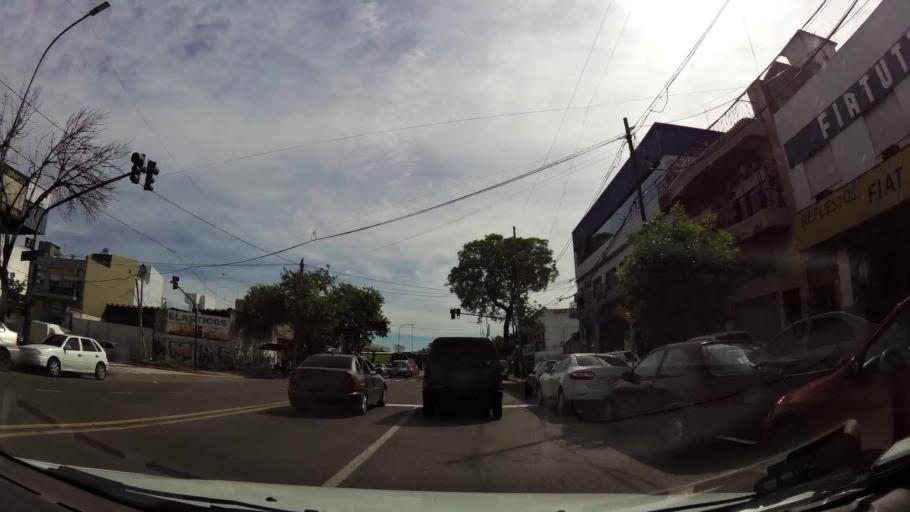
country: AR
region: Buenos Aires F.D.
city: Villa Lugano
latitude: -34.6734
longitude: -58.5006
